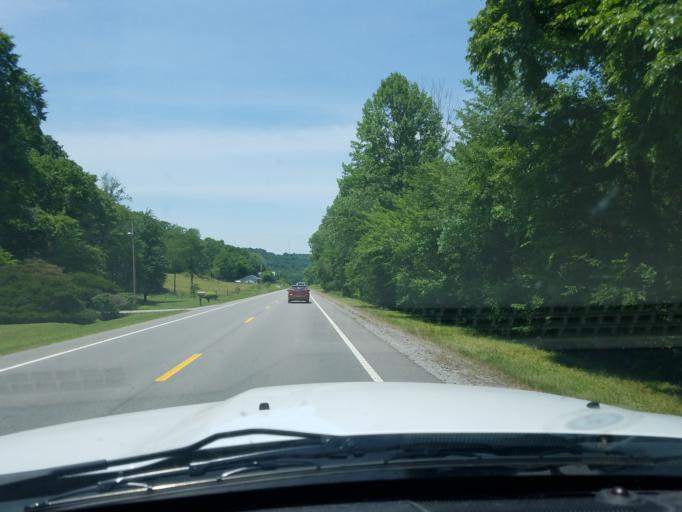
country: US
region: Tennessee
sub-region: Sumner County
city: Westmoreland
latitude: 36.4898
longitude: -86.2726
